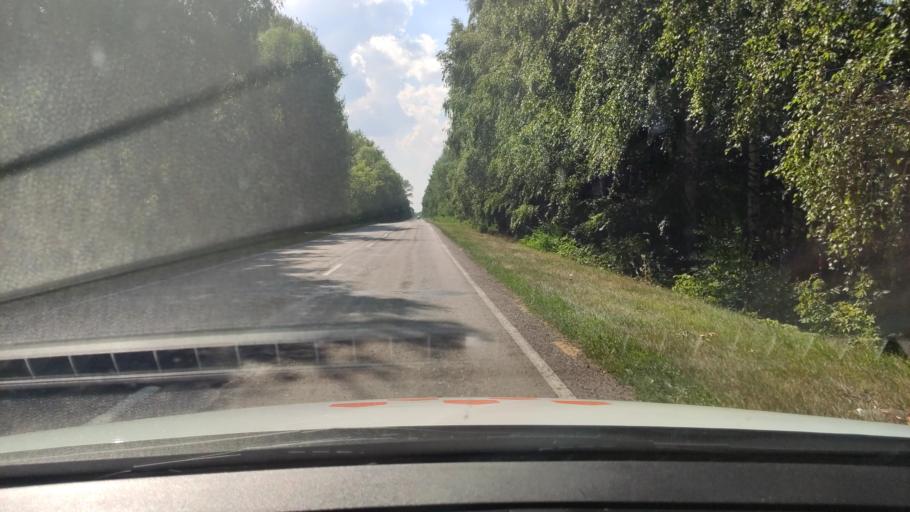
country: RU
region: Voronezj
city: Ertil'
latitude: 51.7831
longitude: 40.5608
